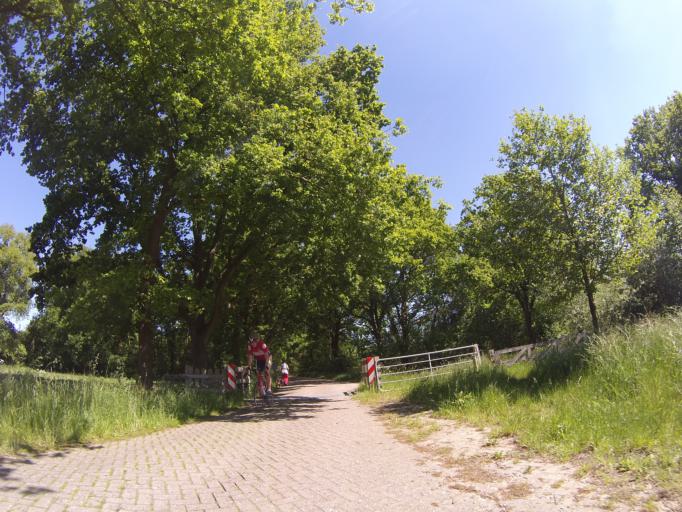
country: NL
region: Drenthe
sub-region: Gemeente Coevorden
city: Dalen
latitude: 52.7546
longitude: 6.6746
